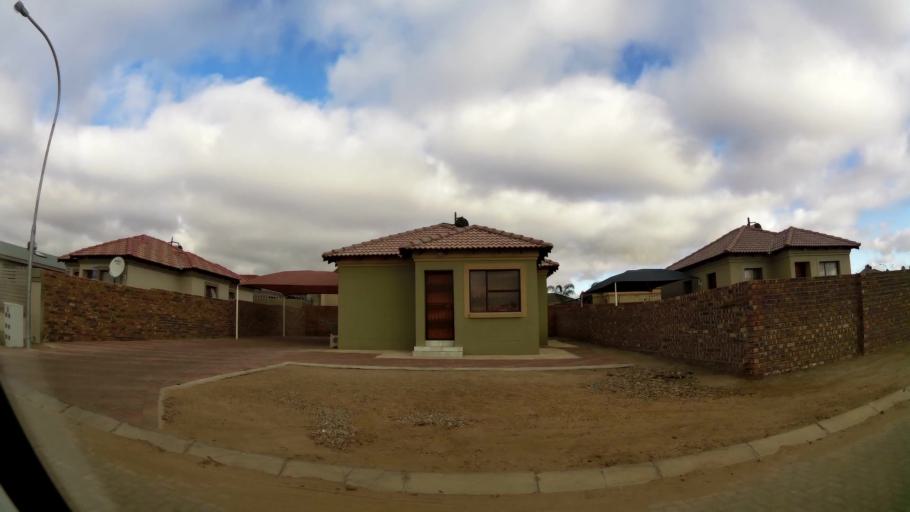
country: ZA
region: Limpopo
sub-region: Capricorn District Municipality
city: Polokwane
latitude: -23.9210
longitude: 29.4463
